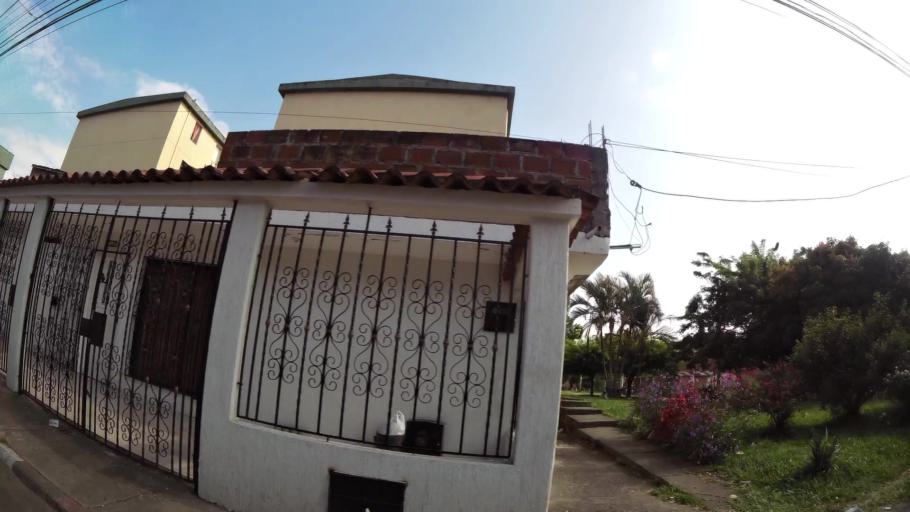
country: CO
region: Valle del Cauca
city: Cali
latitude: 3.4176
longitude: -76.5287
